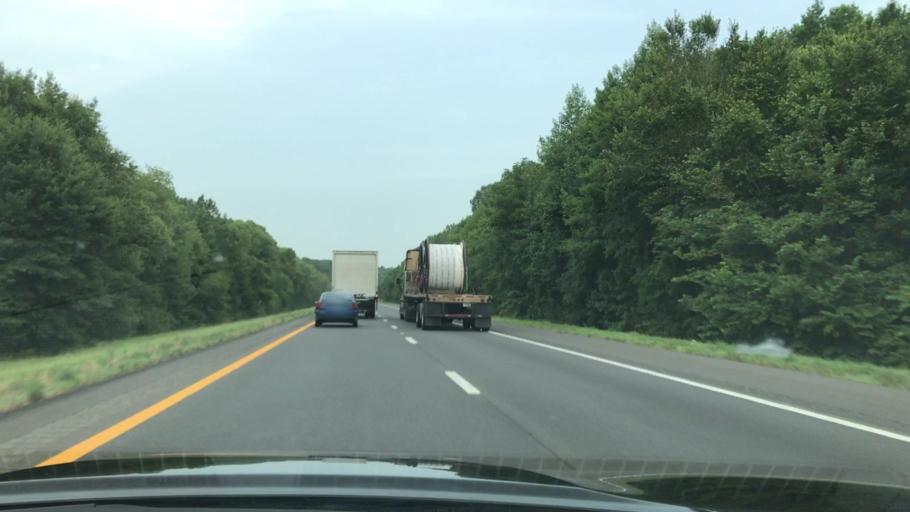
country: US
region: Texas
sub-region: Harrison County
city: Marshall
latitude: 32.4875
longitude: -94.4559
